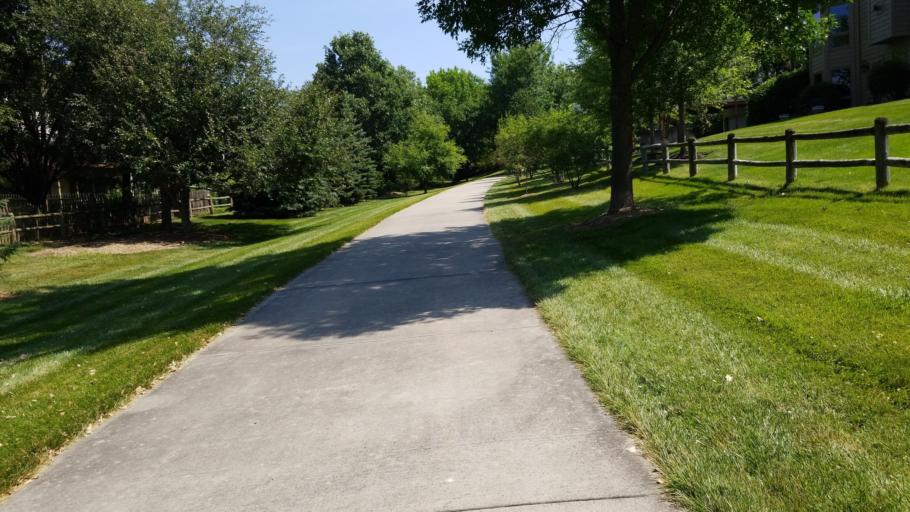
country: US
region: Nebraska
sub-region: Douglas County
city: Elkhorn
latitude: 41.2830
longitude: -96.1633
